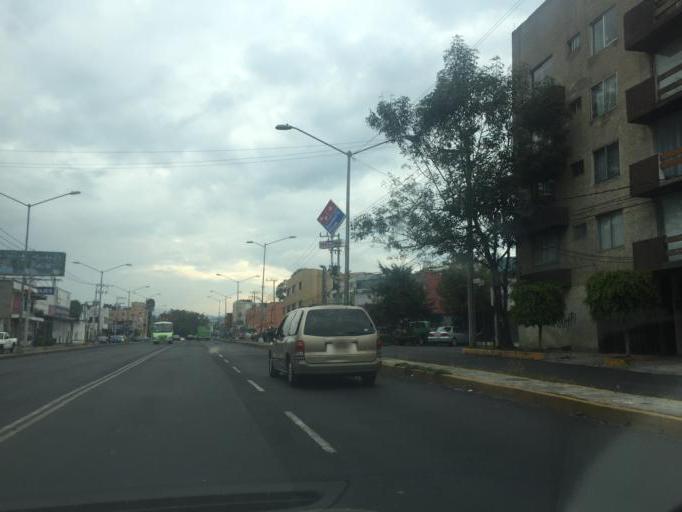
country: MX
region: Mexico City
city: Alvaro Obregon
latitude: 19.3681
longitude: -99.2277
